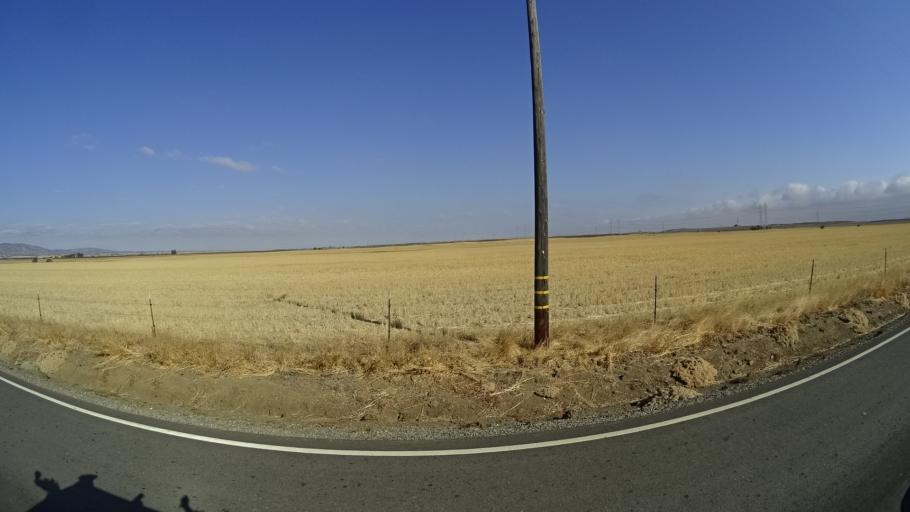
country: US
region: California
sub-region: Yolo County
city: Esparto
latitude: 38.7809
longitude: -122.0218
